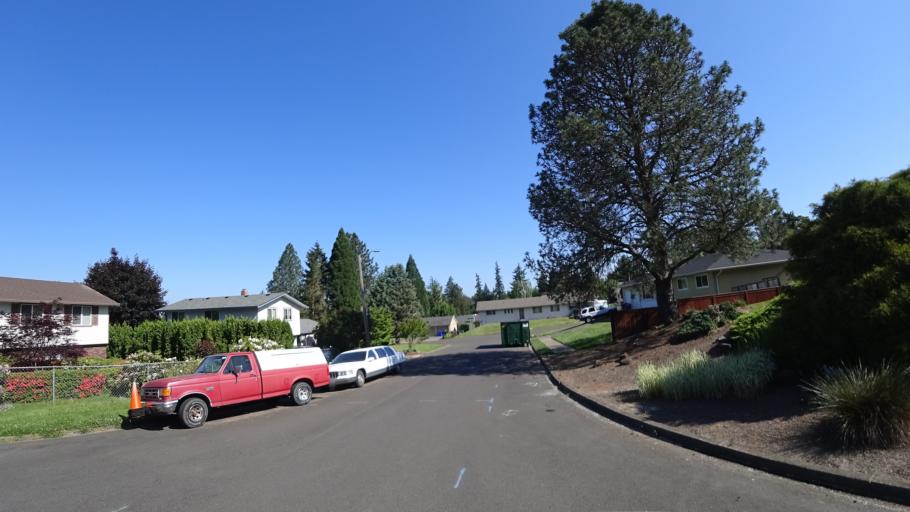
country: US
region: Oregon
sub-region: Multnomah County
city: Lents
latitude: 45.4657
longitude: -122.5546
